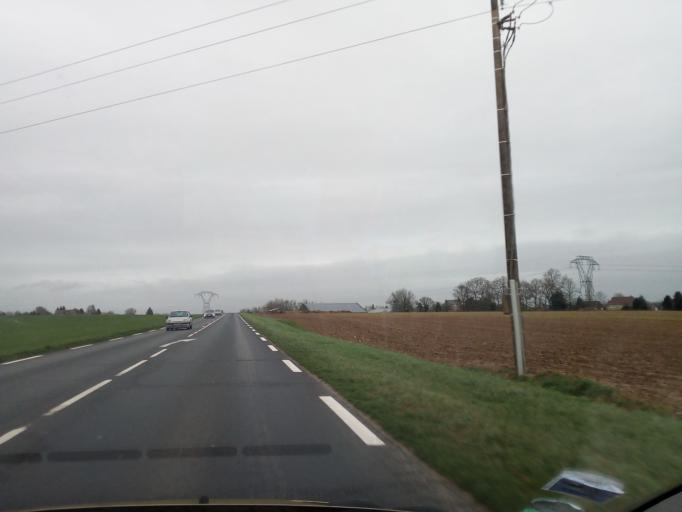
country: FR
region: Haute-Normandie
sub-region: Departement de l'Eure
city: Hauville
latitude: 49.3938
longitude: 0.7980
